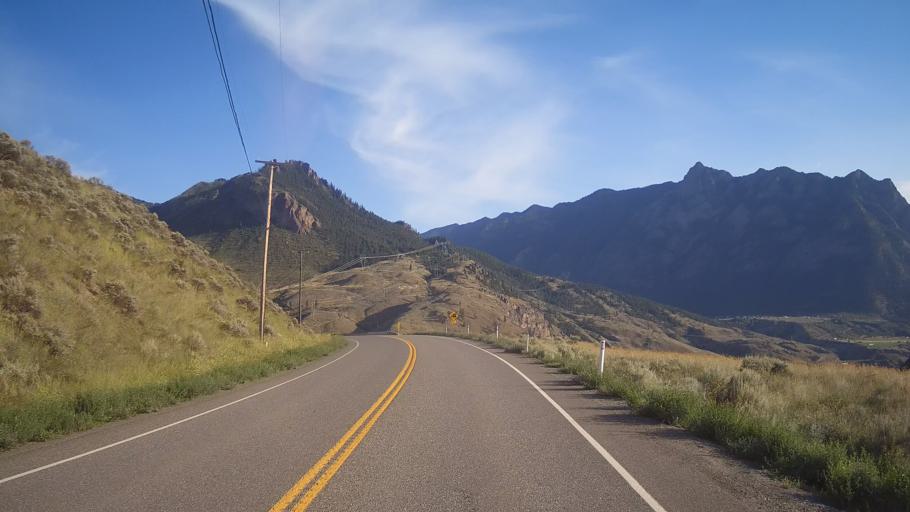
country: CA
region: British Columbia
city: Lillooet
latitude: 50.7636
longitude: -121.8355
